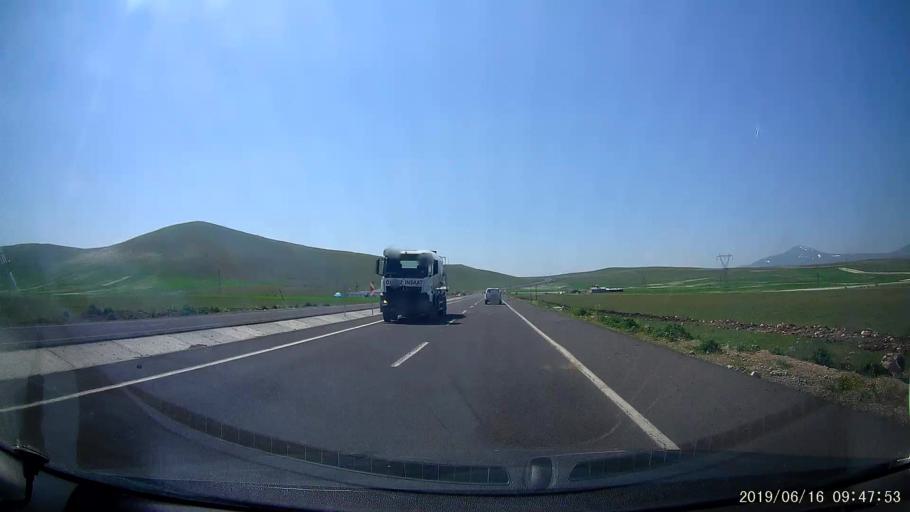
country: TR
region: Kars
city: Digor
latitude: 40.4400
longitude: 43.3487
